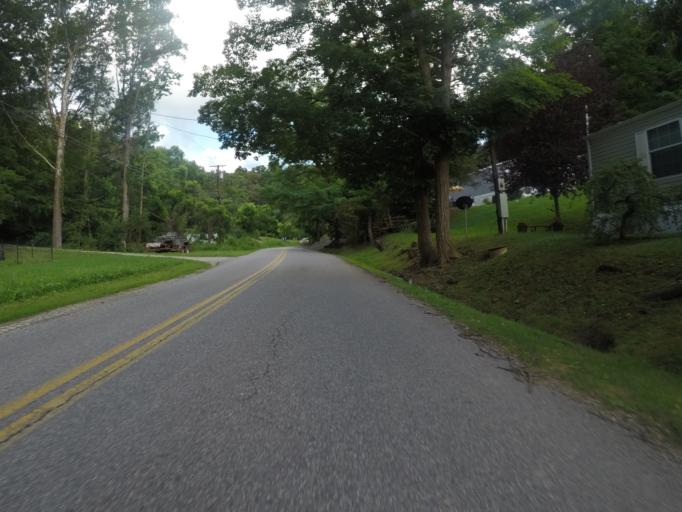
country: US
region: West Virginia
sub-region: Cabell County
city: Pea Ridge
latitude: 38.3935
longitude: -82.3613
